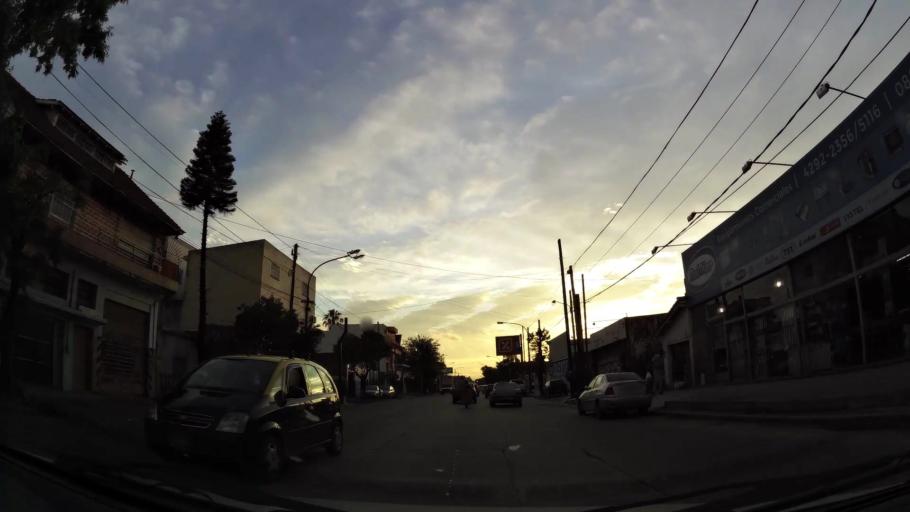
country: AR
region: Buenos Aires
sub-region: Partido de Lomas de Zamora
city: Lomas de Zamora
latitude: -34.7734
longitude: -58.3846
